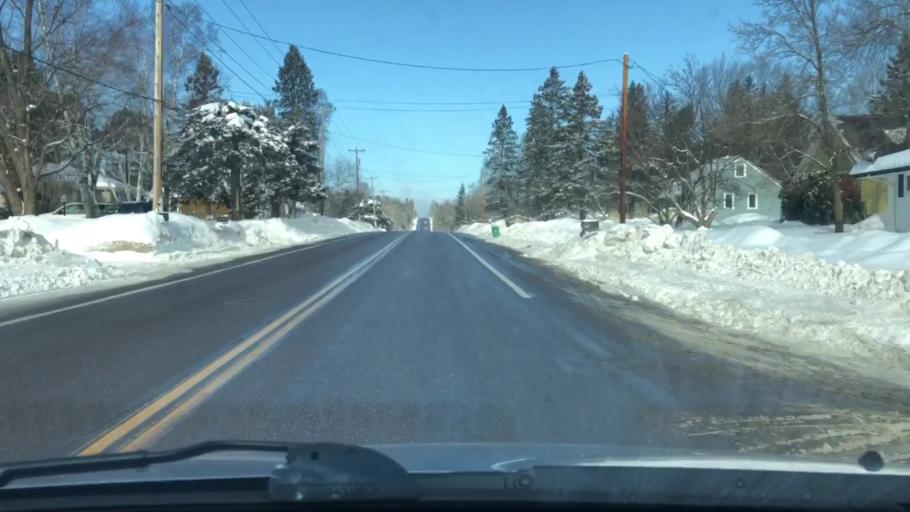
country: US
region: Minnesota
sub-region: Saint Louis County
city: Duluth
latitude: 46.8050
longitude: -92.1322
